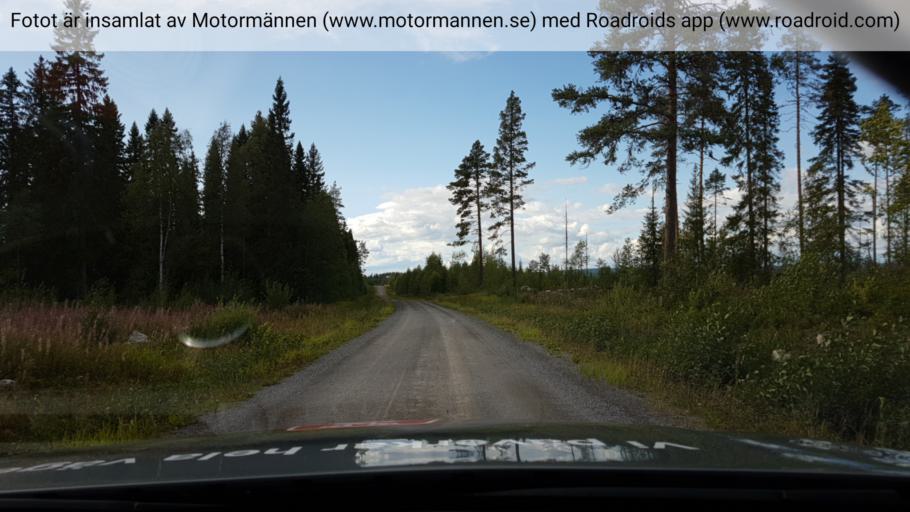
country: SE
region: Jaemtland
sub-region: OEstersunds Kommun
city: Lit
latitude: 63.2967
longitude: 15.3306
